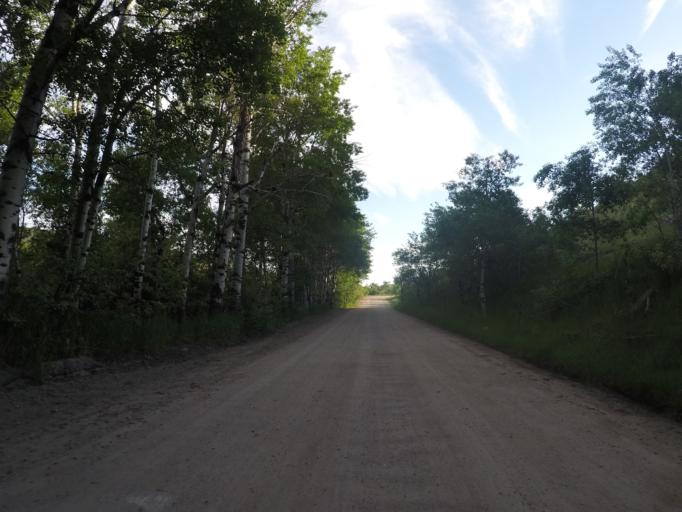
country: US
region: Montana
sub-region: Stillwater County
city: Absarokee
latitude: 45.2926
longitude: -109.5361
